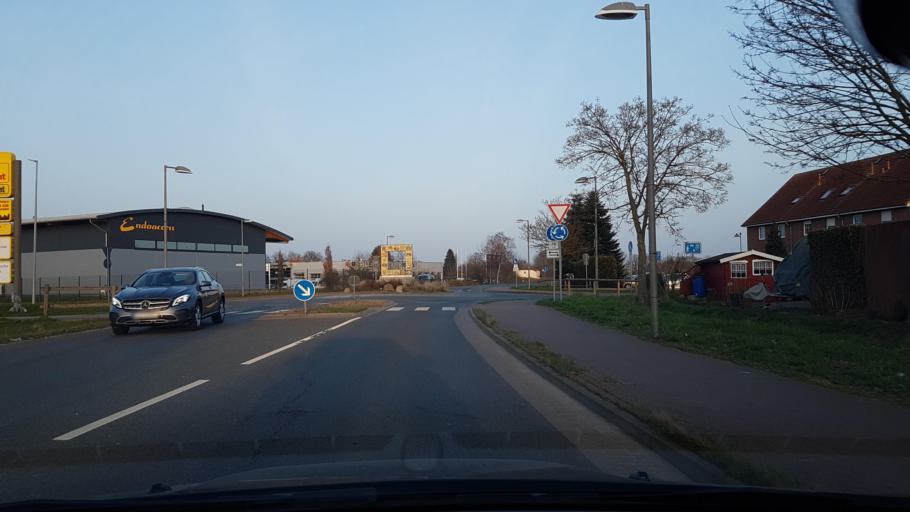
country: DE
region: Lower Saxony
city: Garbsen-Mitte
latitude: 52.4402
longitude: 9.5817
